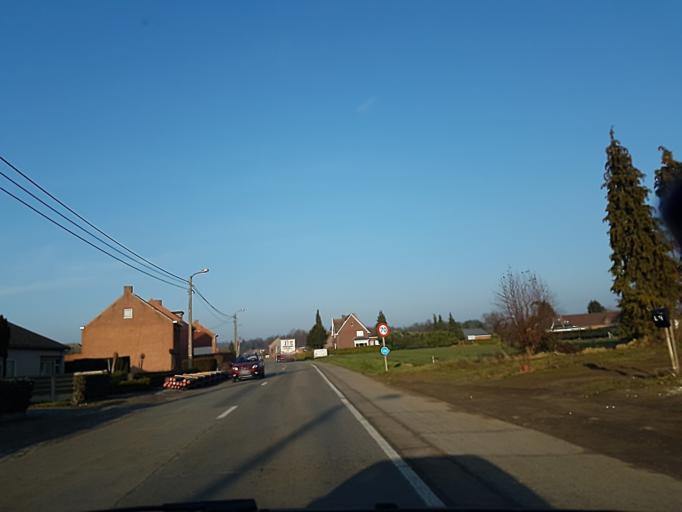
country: BE
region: Flanders
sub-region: Provincie Antwerpen
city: Heist-op-den-Berg
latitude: 51.0619
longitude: 4.7358
